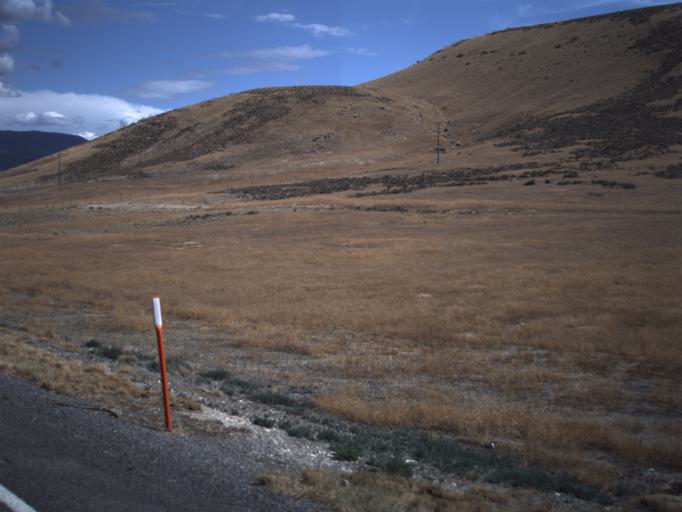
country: US
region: Utah
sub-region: Sanpete County
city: Gunnison
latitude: 39.1564
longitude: -111.7753
